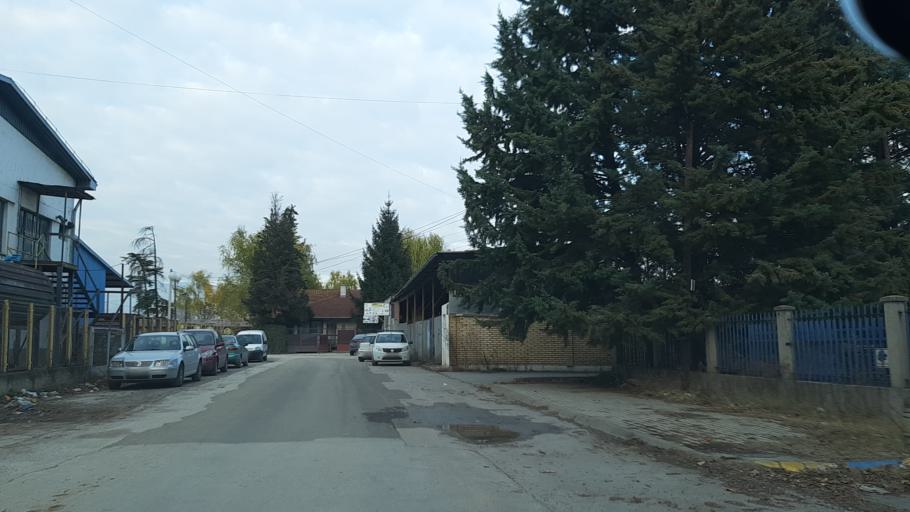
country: MK
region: Kisela Voda
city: Usje
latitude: 41.9796
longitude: 21.4479
